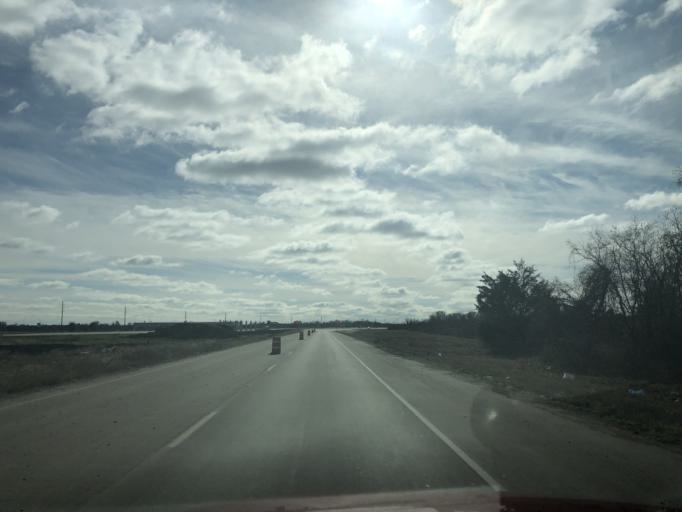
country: US
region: Texas
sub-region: Chambers County
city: Mont Belvieu
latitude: 29.8196
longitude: -94.8641
